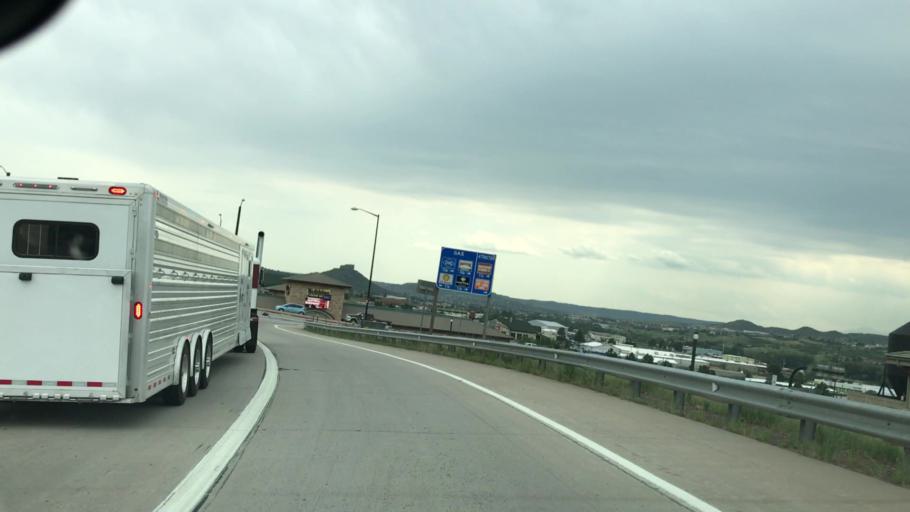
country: US
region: Colorado
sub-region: Douglas County
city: Castle Rock
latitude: 39.4128
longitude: -104.8705
